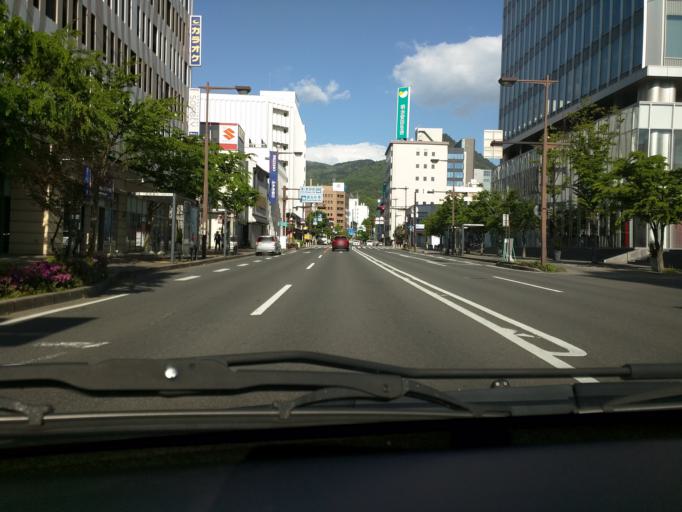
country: JP
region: Nagano
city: Nagano-shi
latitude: 36.6494
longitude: 138.1887
